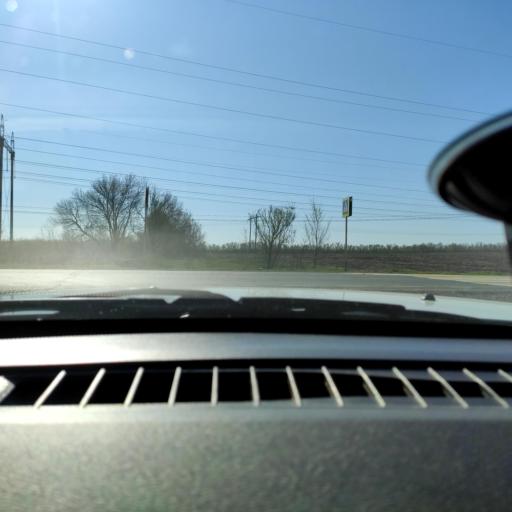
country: RU
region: Samara
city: Dubovyy Umet
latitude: 53.0821
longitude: 50.3906
